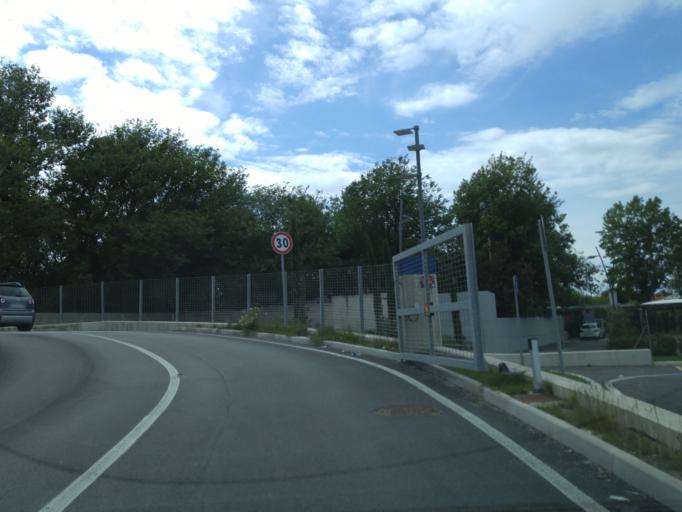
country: IT
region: The Marches
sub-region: Provincia di Pesaro e Urbino
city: Fano
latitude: 43.8335
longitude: 13.0396
